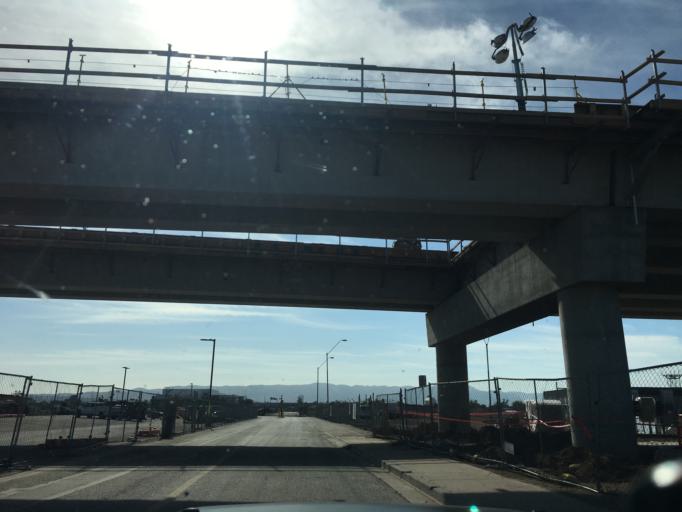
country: US
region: Arizona
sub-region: Maricopa County
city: Phoenix
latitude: 33.4355
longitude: -112.0304
